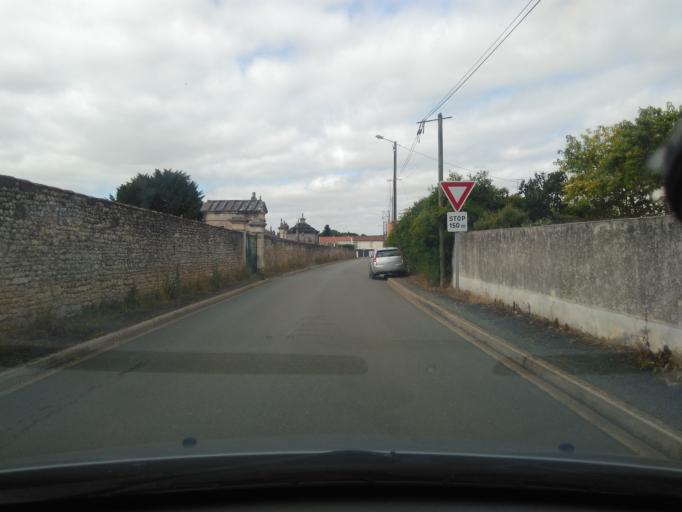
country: FR
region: Pays de la Loire
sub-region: Departement de la Vendee
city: Nalliers
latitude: 46.4721
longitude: -1.0230
